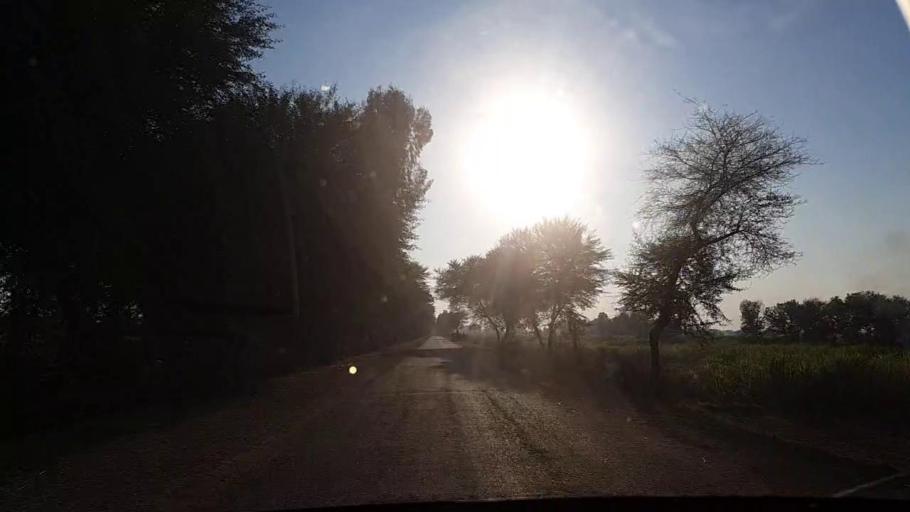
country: PK
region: Sindh
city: Sobhadero
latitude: 27.4173
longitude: 68.4023
